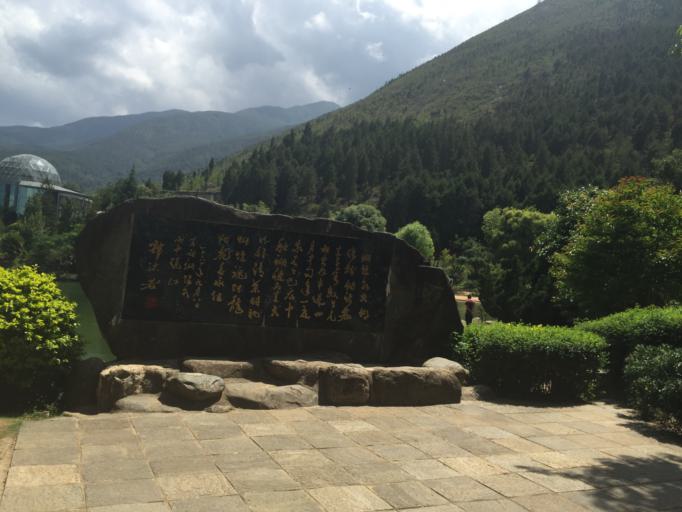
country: CN
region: Yunnan
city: Yuhu
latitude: 25.9090
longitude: 100.0960
